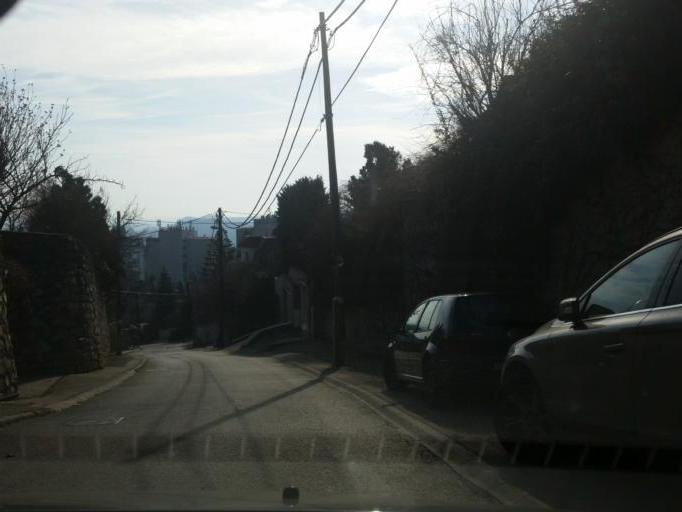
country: HU
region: Budapest
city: Budapest II. keruelet
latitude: 47.5328
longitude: 19.0012
